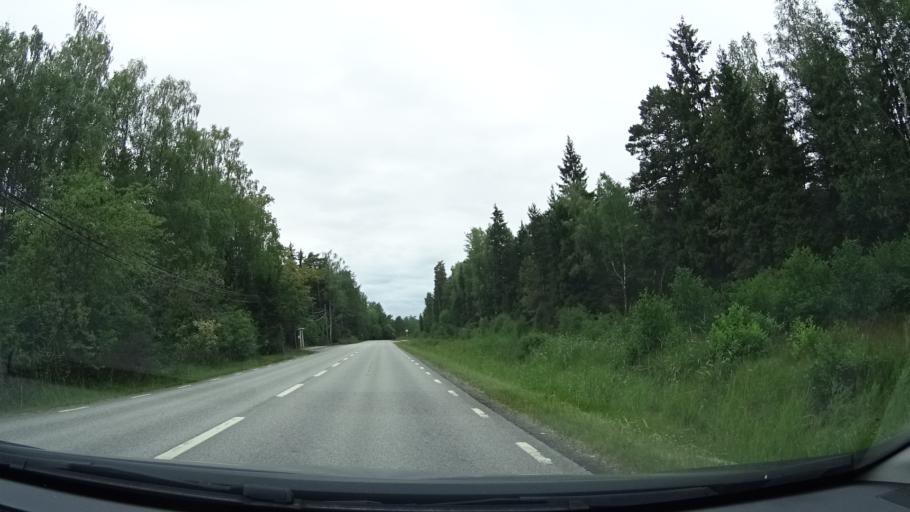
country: SE
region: Stockholm
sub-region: Varmdo Kommun
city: Hemmesta
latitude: 59.3428
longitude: 18.4814
